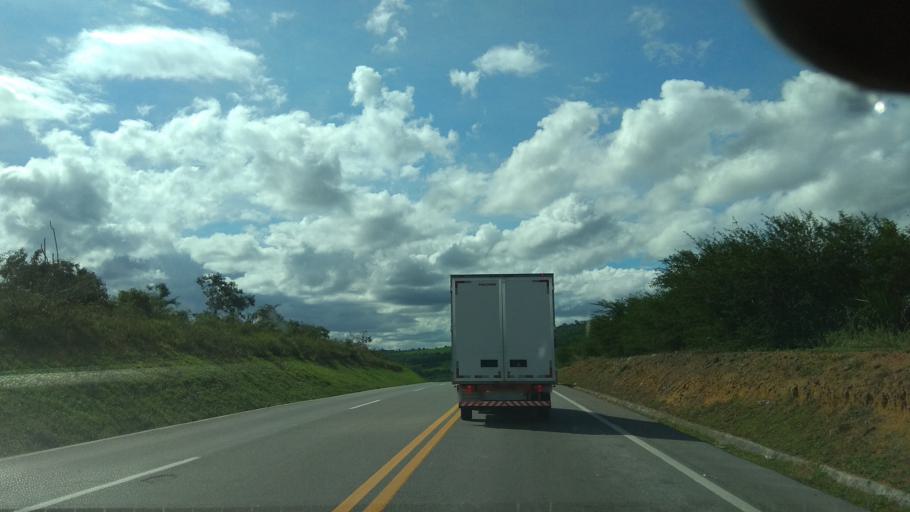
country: BR
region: Bahia
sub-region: Santa Ines
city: Santa Ines
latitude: -13.1695
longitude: -39.9979
